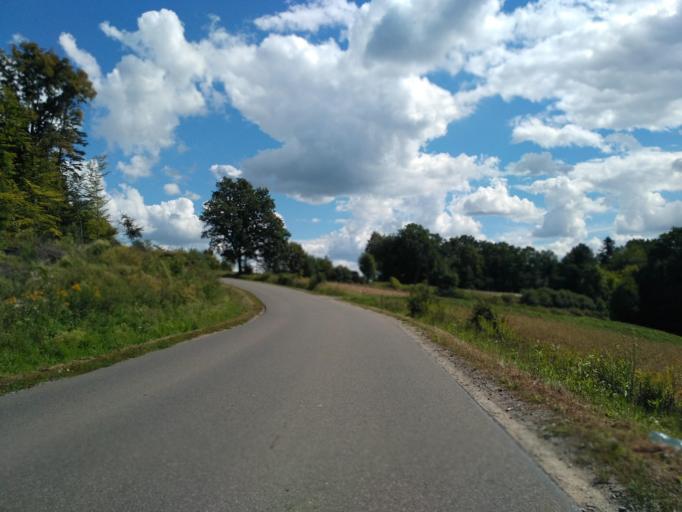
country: PL
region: Subcarpathian Voivodeship
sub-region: Powiat jasielski
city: Trzcinica
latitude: 49.7564
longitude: 21.4085
